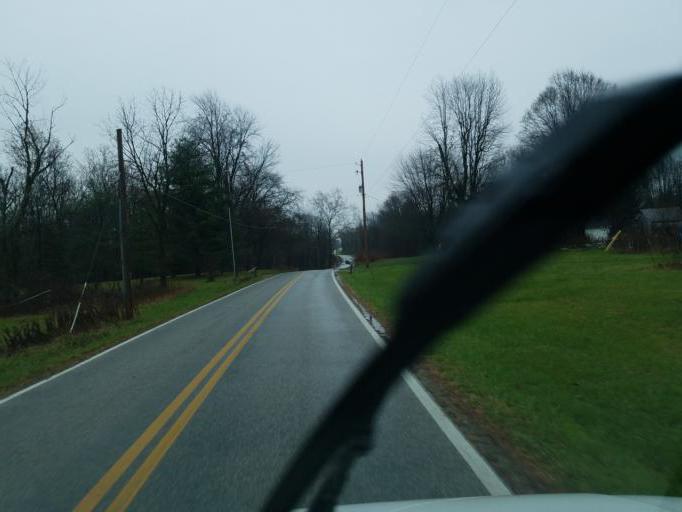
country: US
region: Ohio
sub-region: Delaware County
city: Sunbury
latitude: 40.2877
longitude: -82.7907
